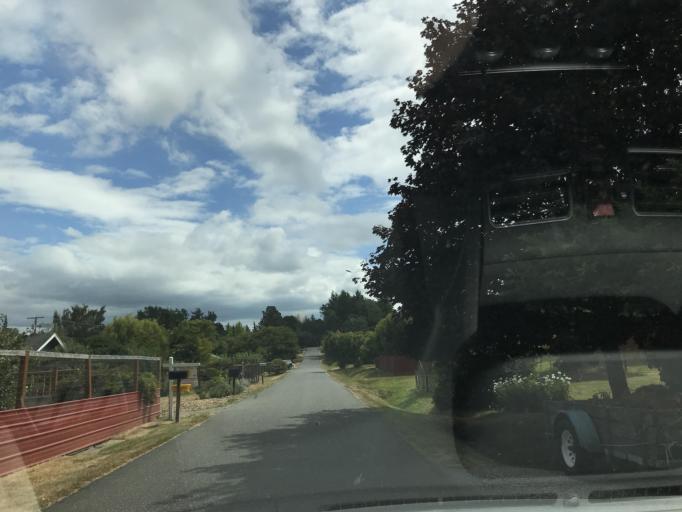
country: US
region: Washington
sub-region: Whatcom County
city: Bellingham
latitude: 48.7160
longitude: -122.5086
